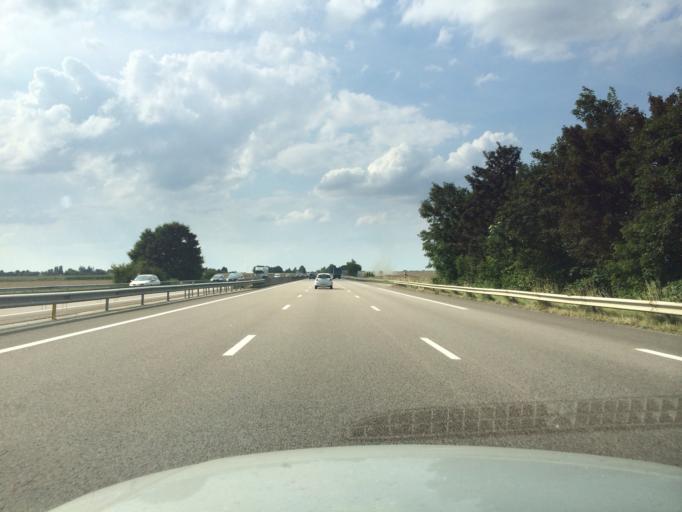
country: FR
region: Haute-Normandie
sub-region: Departement de l'Eure
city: La Chapelle-Reanville
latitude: 49.0667
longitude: 1.4161
